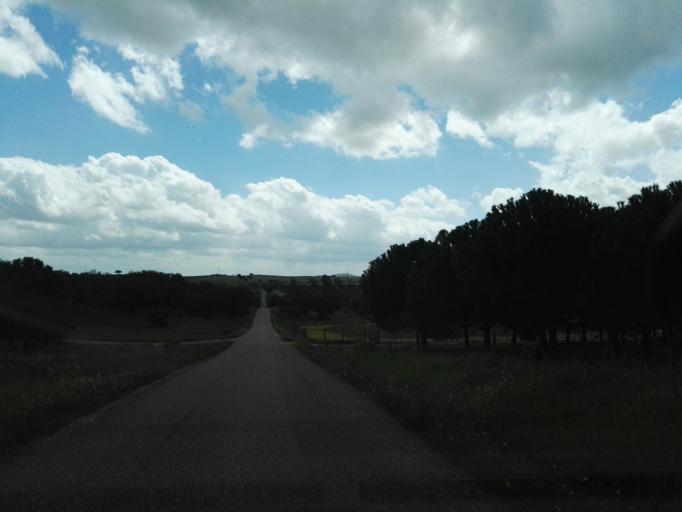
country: PT
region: Portalegre
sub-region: Elvas
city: Elvas
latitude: 38.9782
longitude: -7.1755
